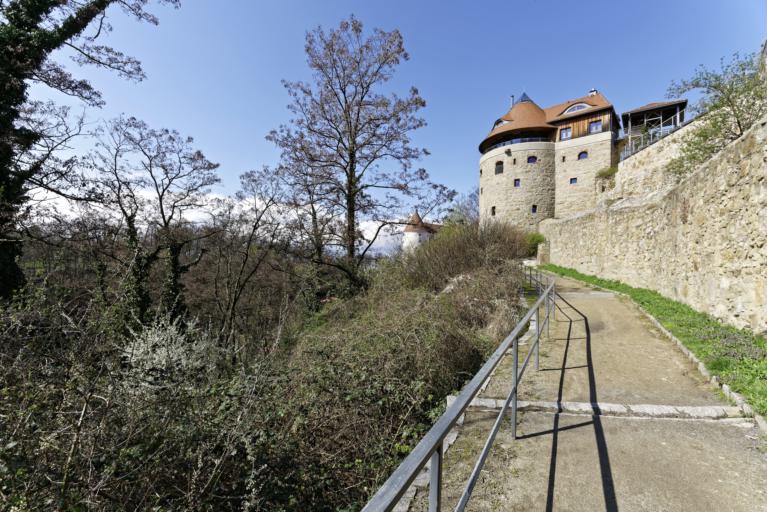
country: DE
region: Saxony
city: Bautzen
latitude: 51.1816
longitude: 14.4203
